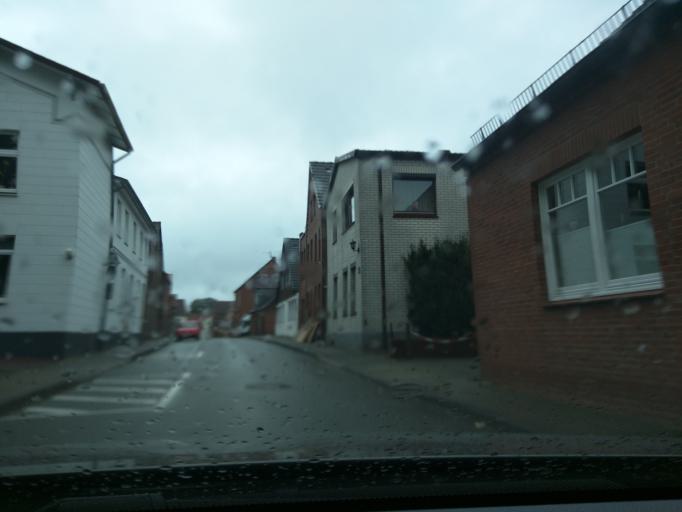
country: DE
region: Schleswig-Holstein
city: Lauenburg
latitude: 53.3725
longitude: 10.5520
